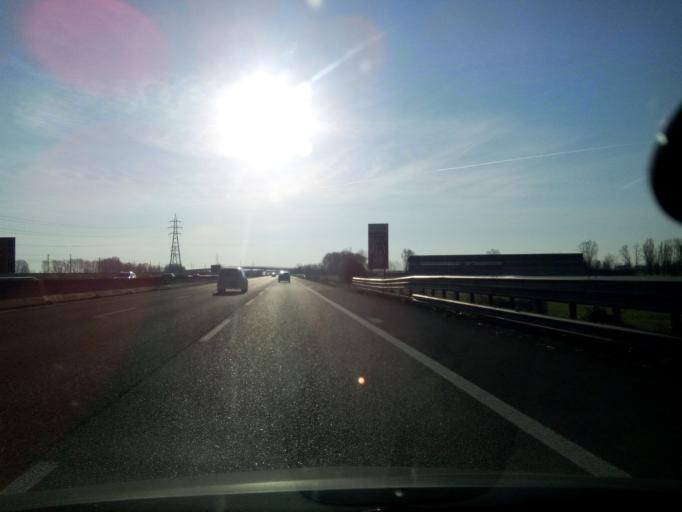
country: IT
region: Emilia-Romagna
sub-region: Provincia di Parma
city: Soragna
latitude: 44.8870
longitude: 10.1039
